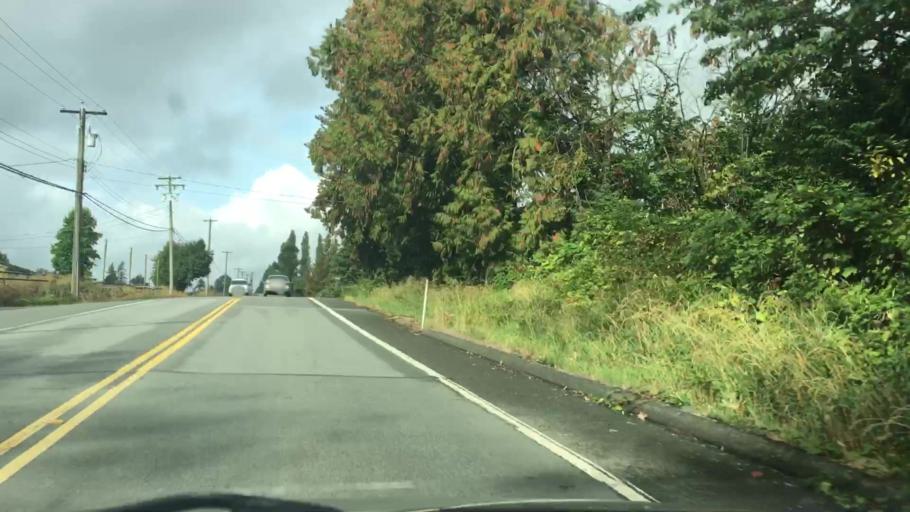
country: CA
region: British Columbia
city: Langley
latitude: 49.1042
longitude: -122.5870
